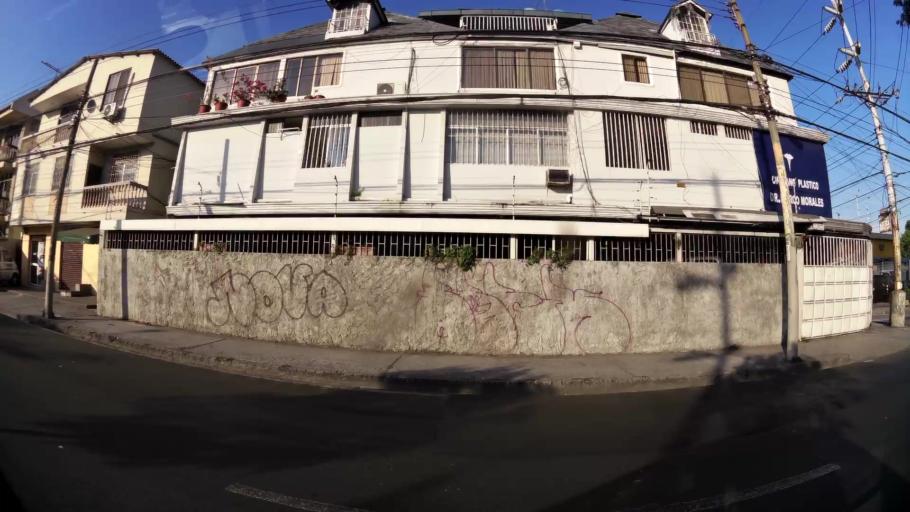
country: EC
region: Guayas
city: Guayaquil
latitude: -2.1771
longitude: -79.8977
